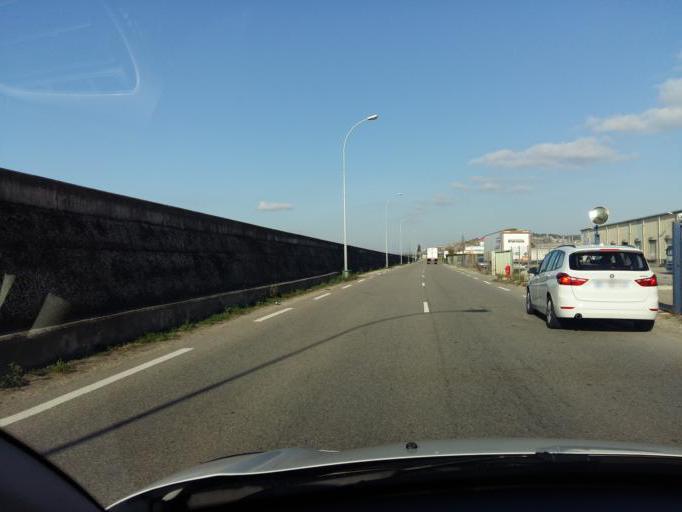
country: FR
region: Provence-Alpes-Cote d'Azur
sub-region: Departement du Vaucluse
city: Cavaillon
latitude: 43.8134
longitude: 5.0425
